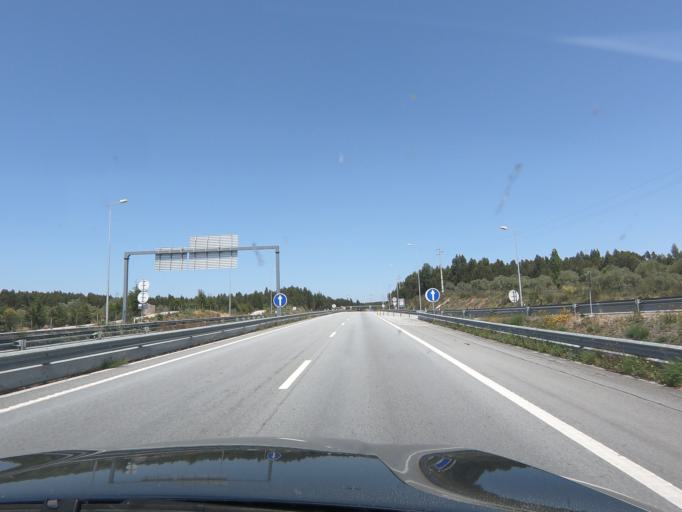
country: PT
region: Santarem
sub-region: Entroncamento
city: Entroncamento
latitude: 39.4953
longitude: -8.4422
